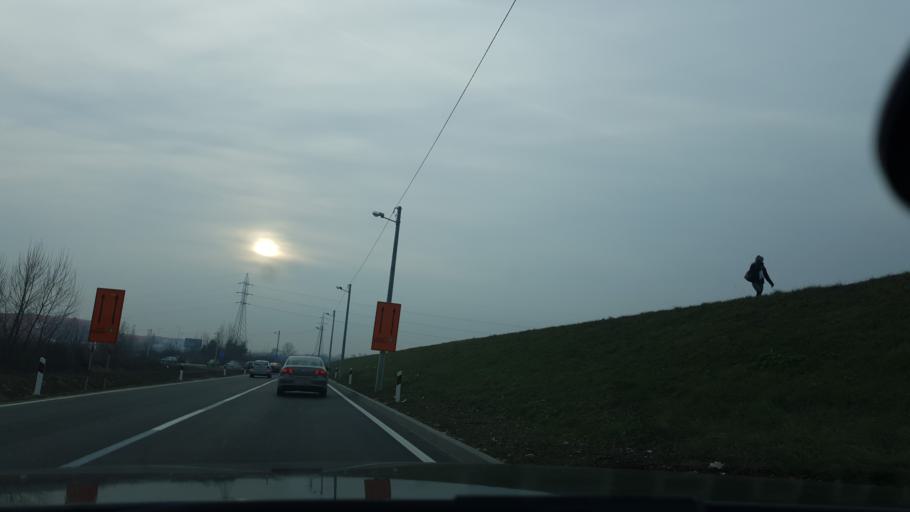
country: HR
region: Grad Zagreb
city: Novi Zagreb
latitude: 45.7762
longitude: 15.9439
